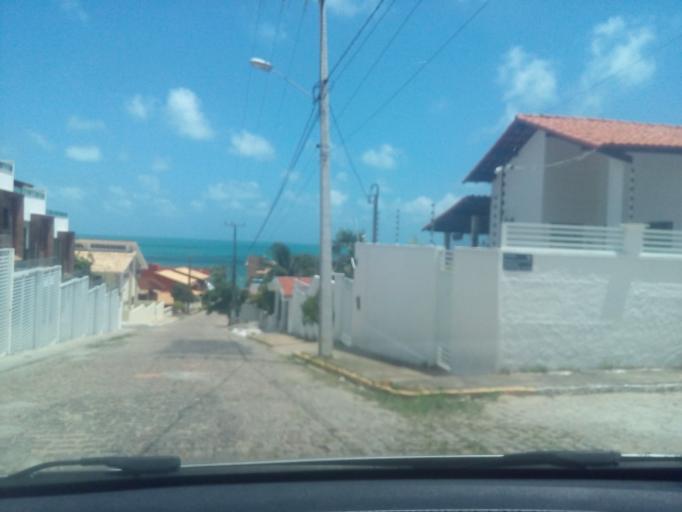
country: BR
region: Rio Grande do Norte
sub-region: Parnamirim
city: Parnamirim
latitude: -5.9686
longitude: -35.1309
